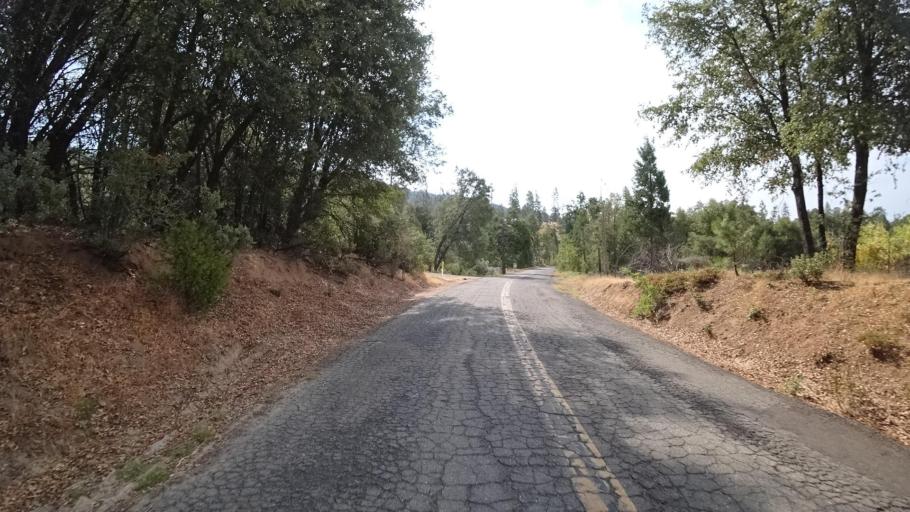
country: US
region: California
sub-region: Mariposa County
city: Midpines
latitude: 37.5002
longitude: -119.7995
